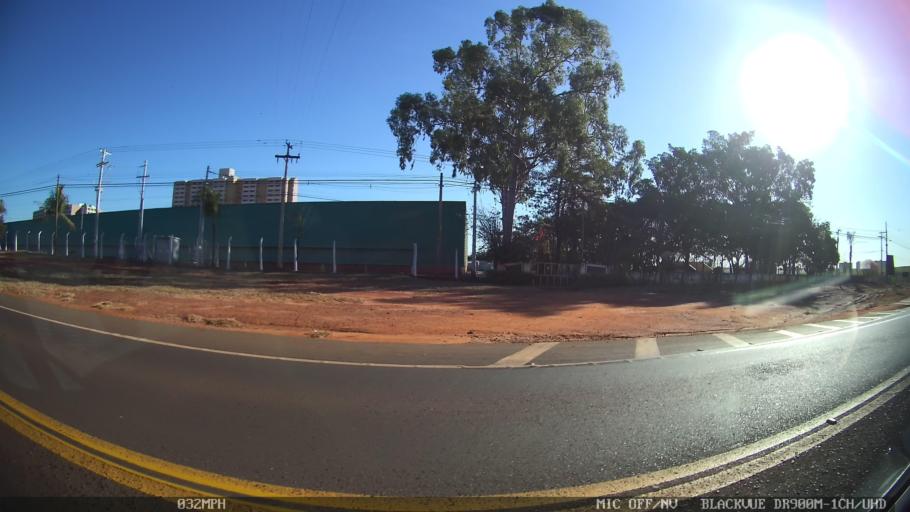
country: BR
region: Sao Paulo
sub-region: Olimpia
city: Olimpia
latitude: -20.7127
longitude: -48.9092
